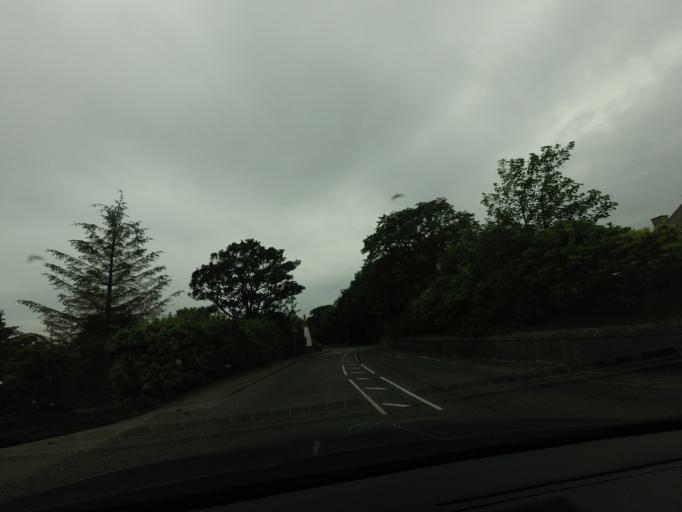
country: GB
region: Scotland
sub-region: Aberdeenshire
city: Portsoy
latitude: 57.6793
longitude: -2.6874
